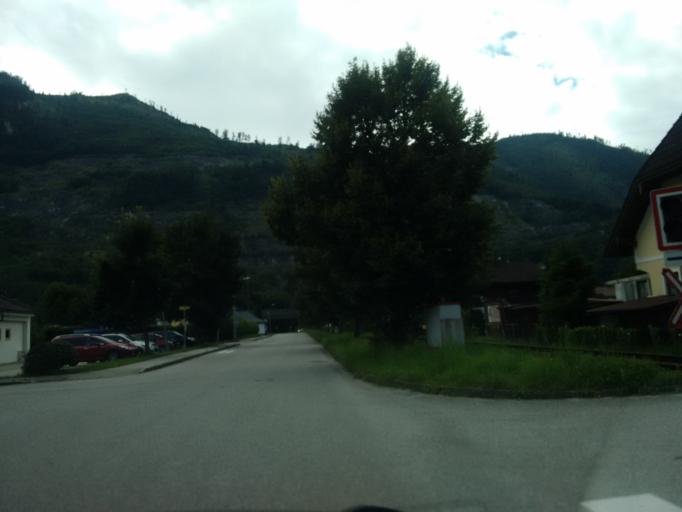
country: AT
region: Upper Austria
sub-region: Politischer Bezirk Gmunden
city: Ebensee
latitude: 47.7983
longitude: 13.7733
